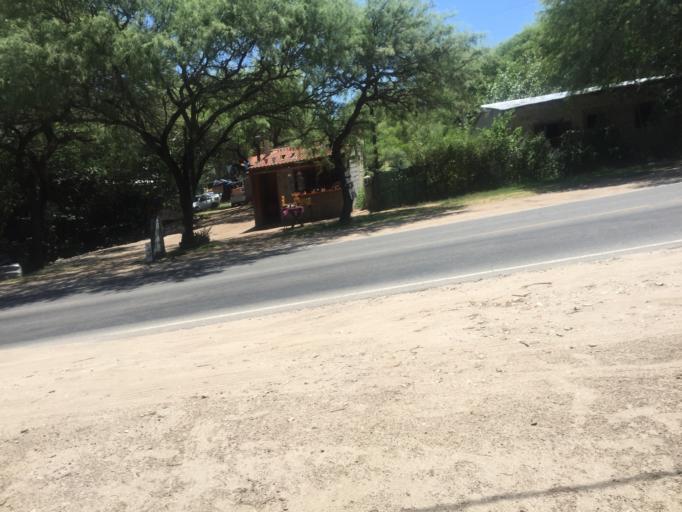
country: AR
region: Cordoba
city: Villa Las Rosas
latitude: -31.9265
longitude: -65.0393
